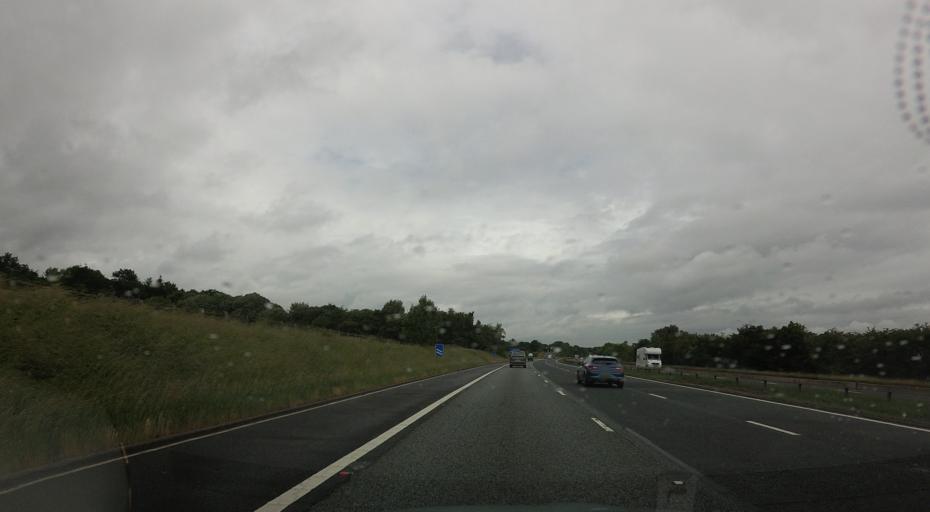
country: GB
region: England
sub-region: Cumbria
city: Scotby
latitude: 54.7911
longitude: -2.8666
